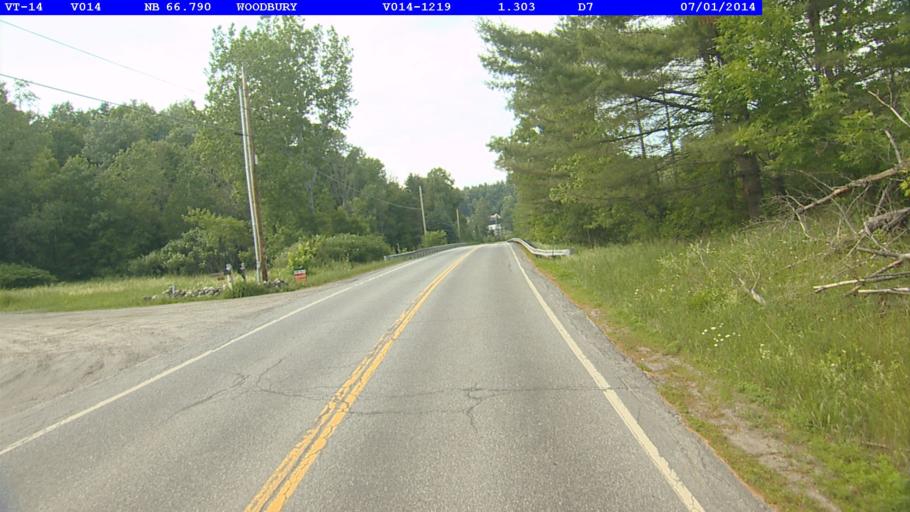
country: US
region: Vermont
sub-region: Caledonia County
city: Hardwick
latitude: 44.4100
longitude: -72.4192
